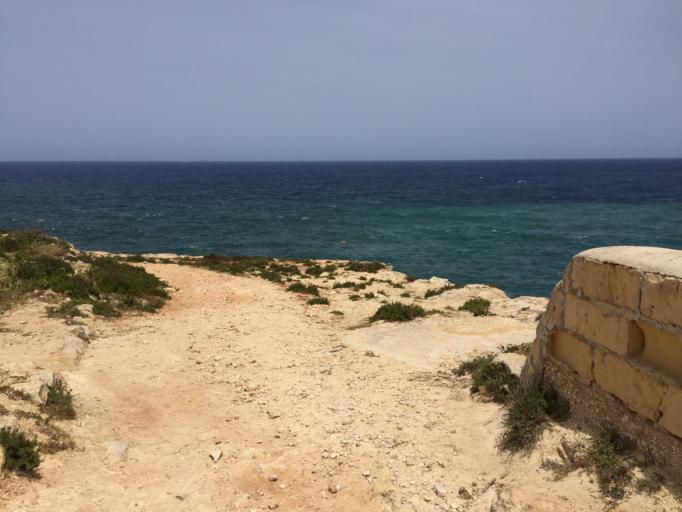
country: MT
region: Ix-Xghajra
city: Xghajra
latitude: 35.8811
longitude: 14.5571
